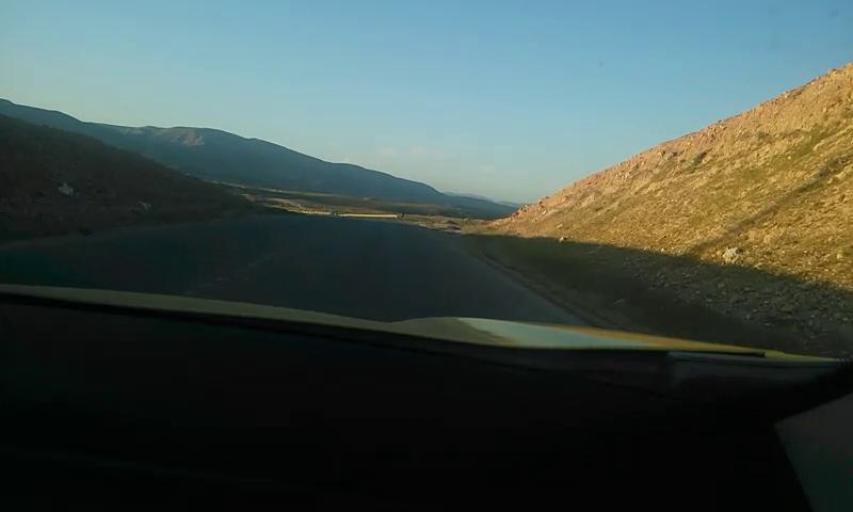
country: PS
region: West Bank
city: An Nuway`imah
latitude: 31.9048
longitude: 35.4242
